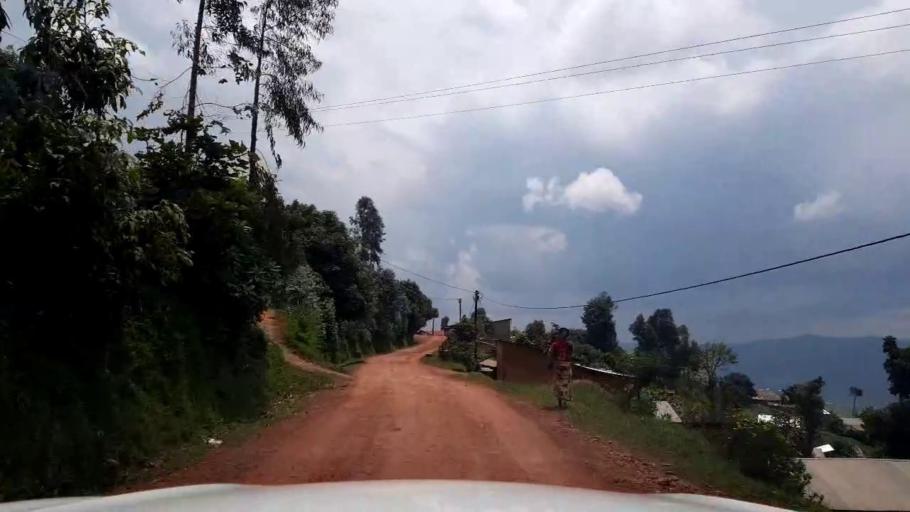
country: RW
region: Northern Province
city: Byumba
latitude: -1.4919
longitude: 29.9293
